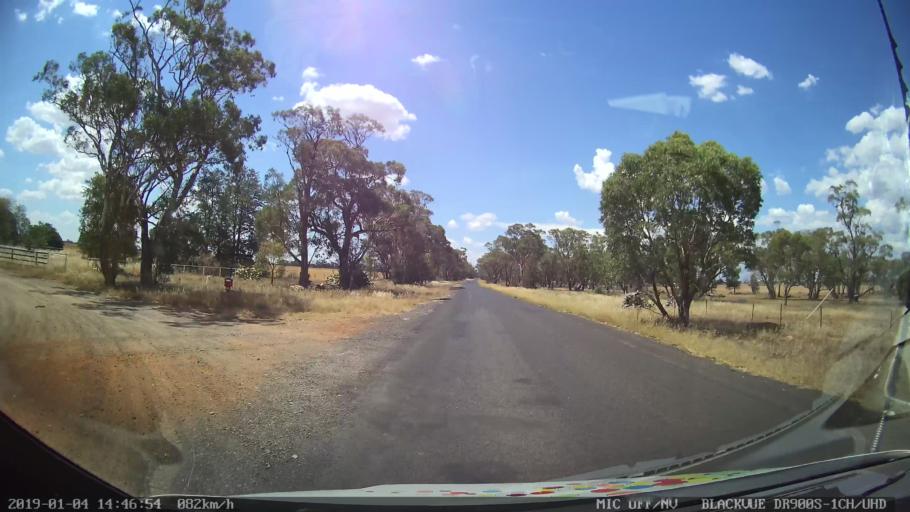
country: AU
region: New South Wales
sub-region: Dubbo Municipality
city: Dubbo
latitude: -32.0757
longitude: 148.6592
